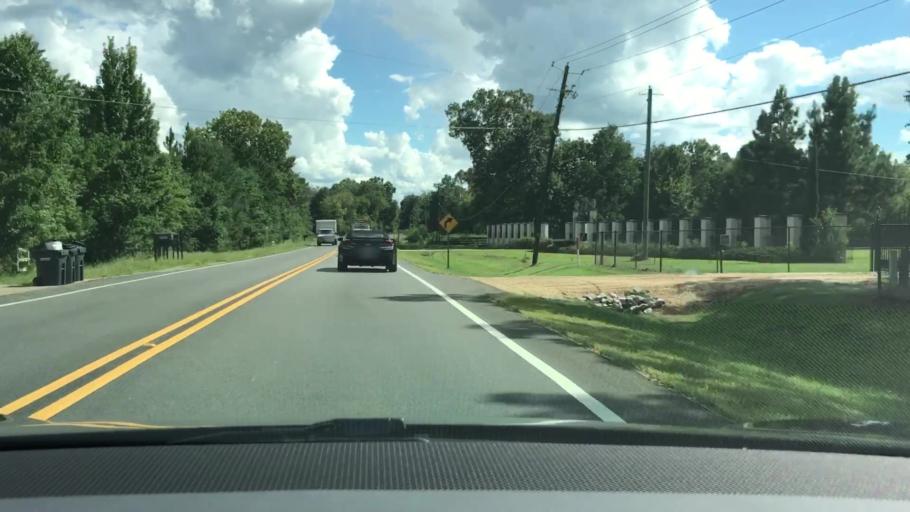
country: US
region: Alabama
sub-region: Montgomery County
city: Pike Road
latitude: 32.3216
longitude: -86.0945
